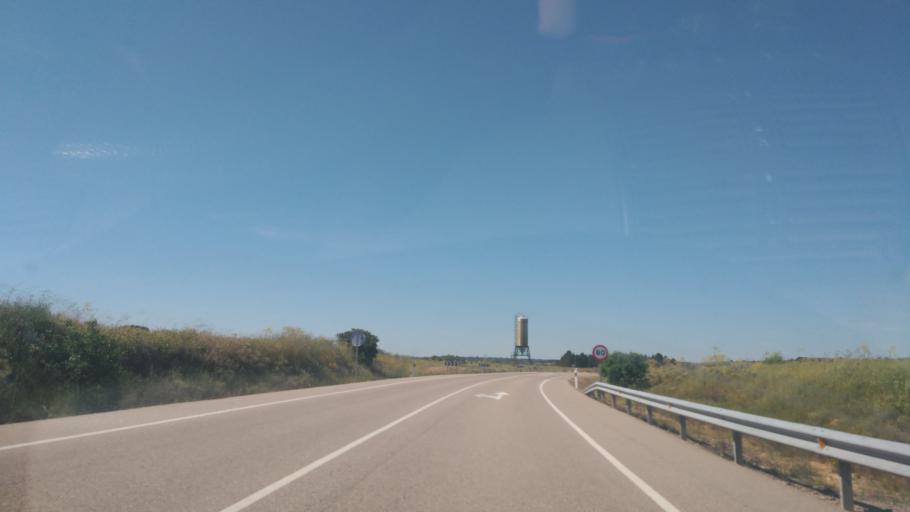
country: ES
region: Castille and Leon
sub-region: Provincia de Zamora
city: Cuelgamures
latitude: 41.2437
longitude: -5.7072
